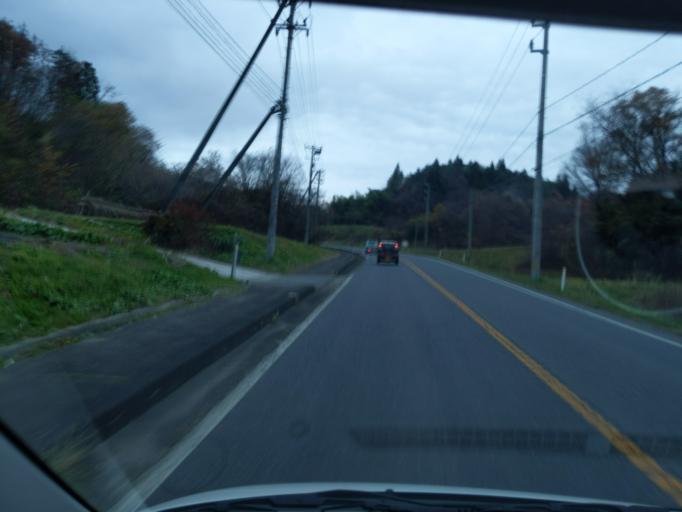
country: JP
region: Iwate
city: Ichinoseki
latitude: 39.0145
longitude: 141.3285
